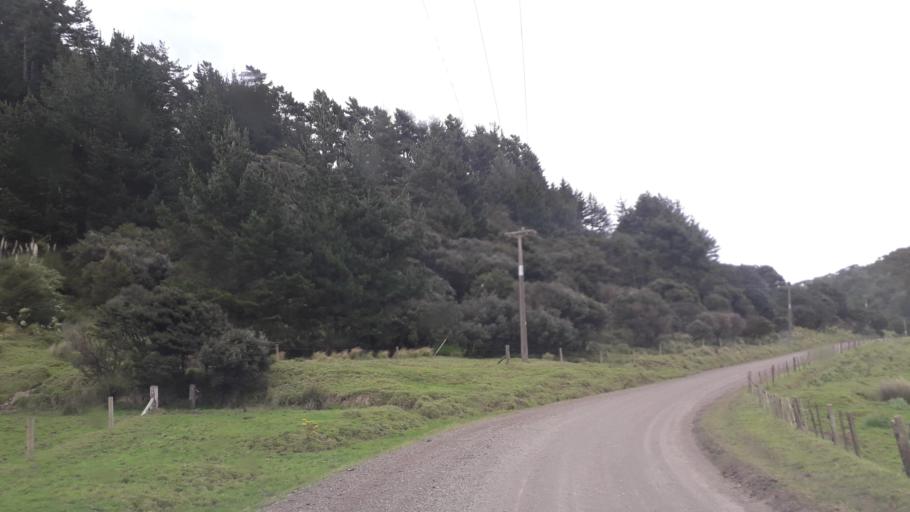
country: NZ
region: Northland
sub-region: Far North District
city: Ahipara
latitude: -35.4411
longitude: 173.3256
